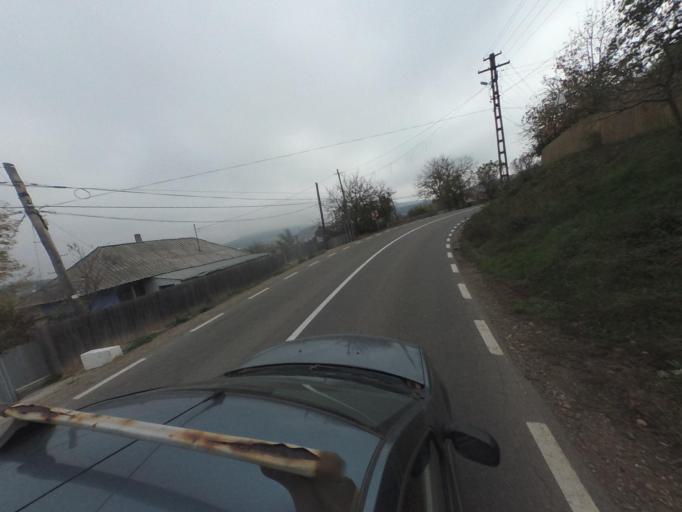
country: RO
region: Vaslui
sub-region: Comuna Bacesti
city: Bacesti
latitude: 46.8289
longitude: 27.2409
